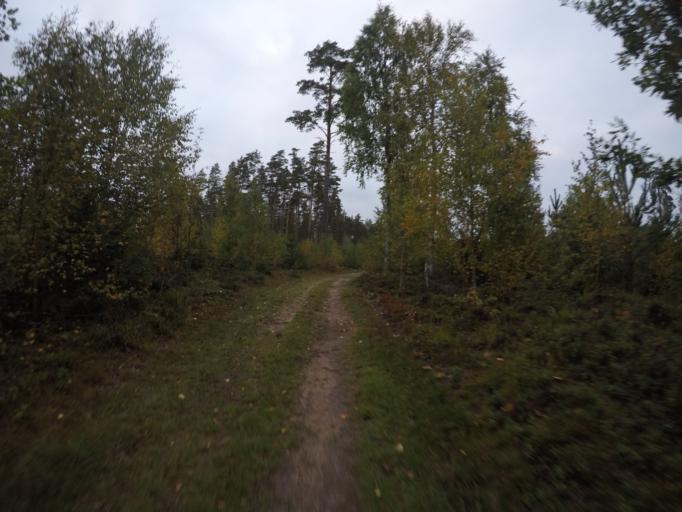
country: SE
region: Vaestmanland
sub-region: Kungsors Kommun
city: Kungsoer
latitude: 59.3719
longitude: 16.1150
